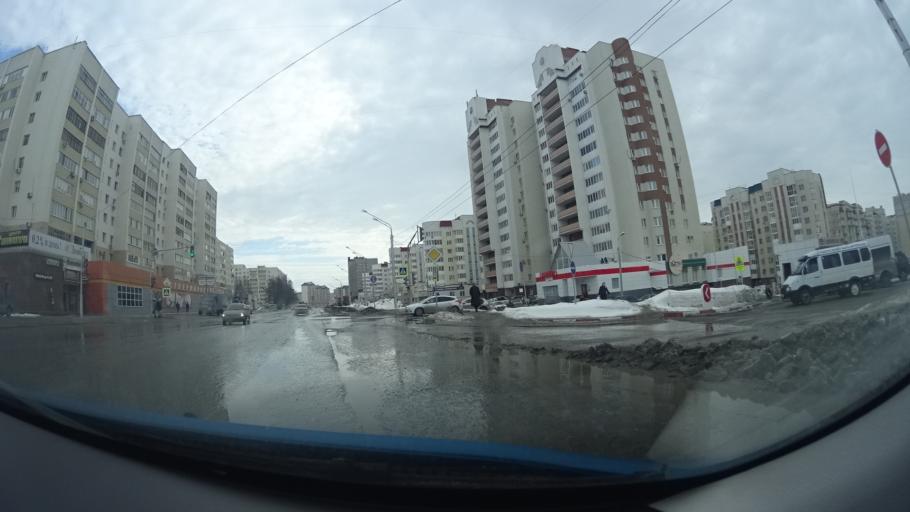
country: RU
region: Bashkortostan
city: Ufa
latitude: 54.6992
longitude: 55.9846
